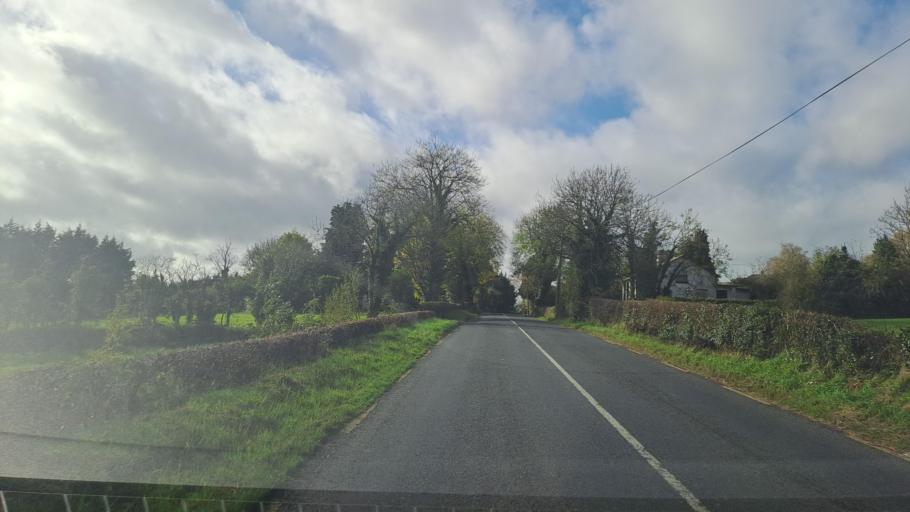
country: IE
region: Ulster
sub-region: An Cabhan
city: Cootehill
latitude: 54.1082
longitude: -6.9704
